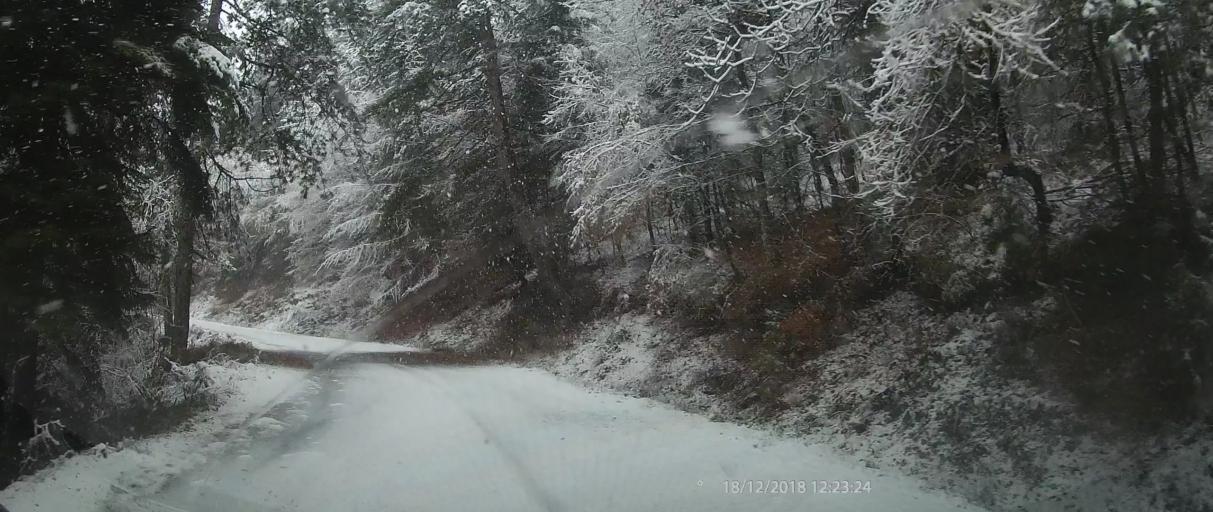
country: GR
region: Central Macedonia
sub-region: Nomos Pierias
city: Litochoro
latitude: 40.0925
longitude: 22.4194
